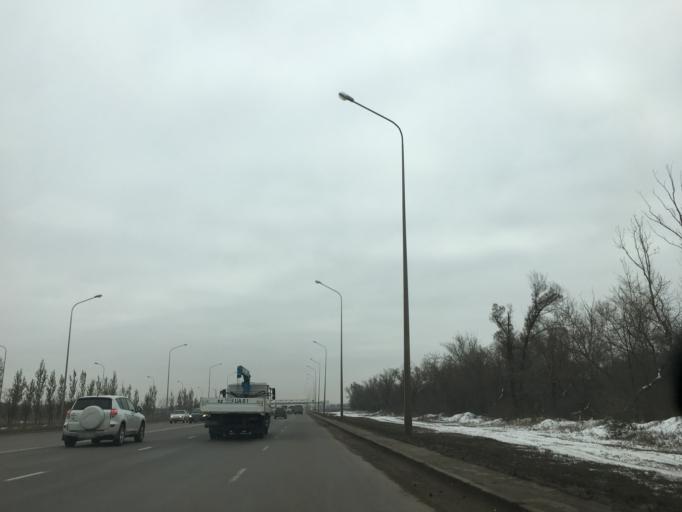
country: KZ
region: Astana Qalasy
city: Astana
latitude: 51.1637
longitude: 71.5098
